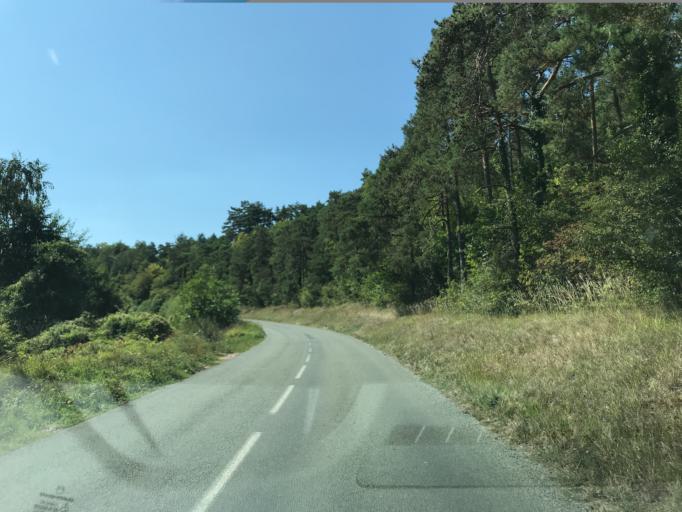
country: FR
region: Haute-Normandie
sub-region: Departement de l'Eure
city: Heudreville-sur-Eure
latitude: 49.1017
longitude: 1.2222
